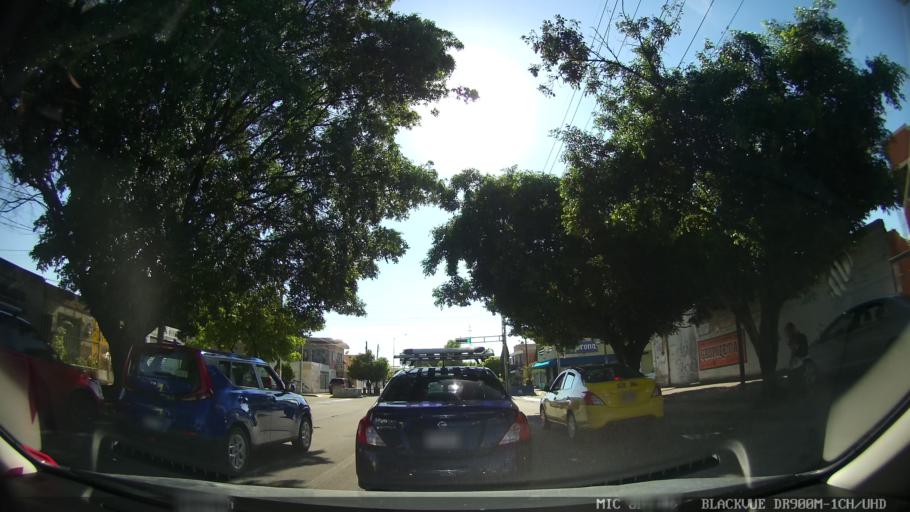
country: MX
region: Jalisco
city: Tlaquepaque
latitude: 20.6632
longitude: -103.2922
